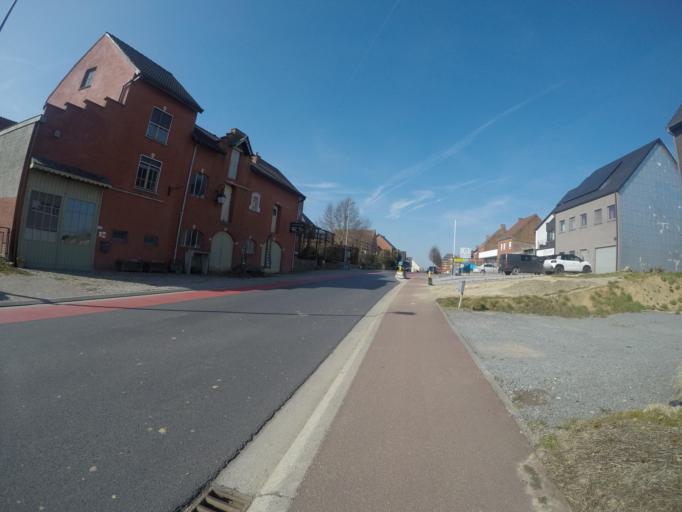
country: BE
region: Flanders
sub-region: Provincie Oost-Vlaanderen
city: Sint-Maria-Lierde
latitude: 50.7839
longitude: 3.8452
